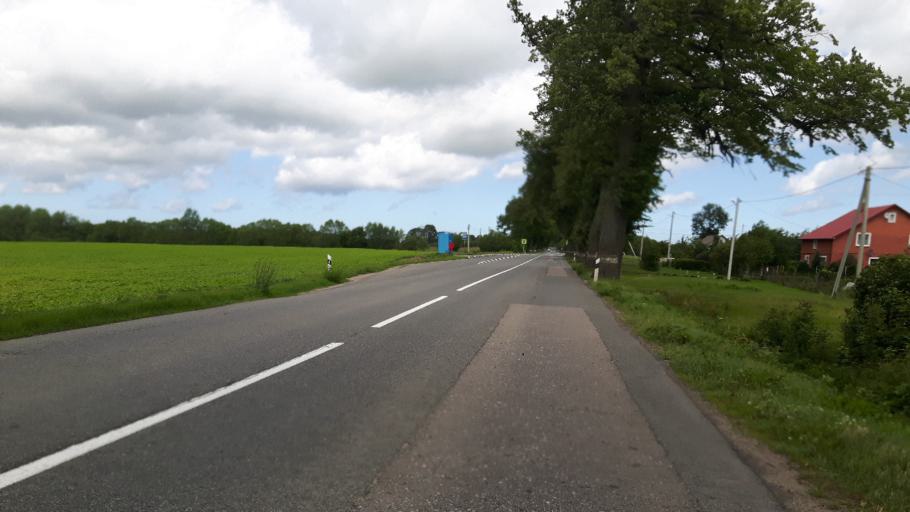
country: RU
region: Kaliningrad
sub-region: Zelenogradskiy Rayon
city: Zelenogradsk
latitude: 54.8579
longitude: 20.4182
